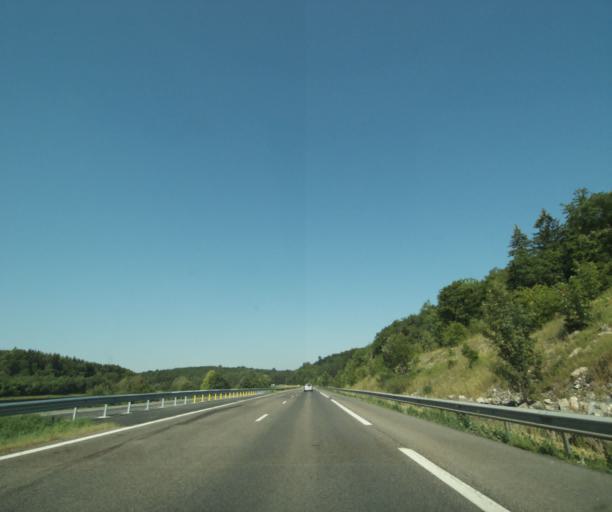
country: FR
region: Lorraine
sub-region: Departement de la Meuse
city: Vacon
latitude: 48.6873
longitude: 5.5707
